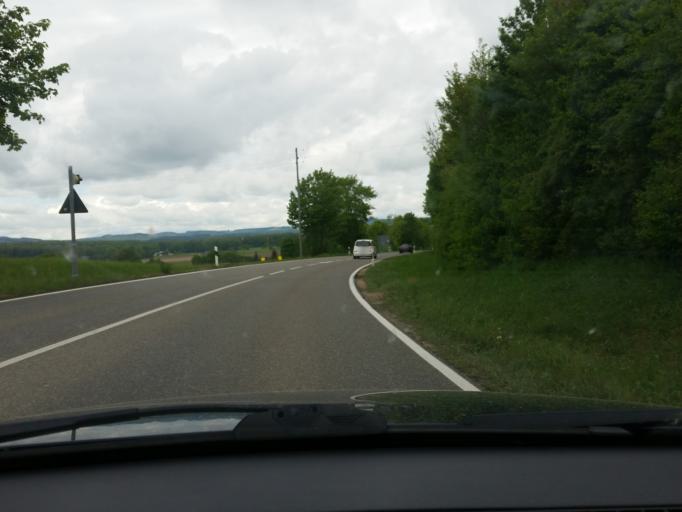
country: DE
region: Baden-Wuerttemberg
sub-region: Freiburg Region
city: Hilzingen
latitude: 47.7613
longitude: 8.7478
